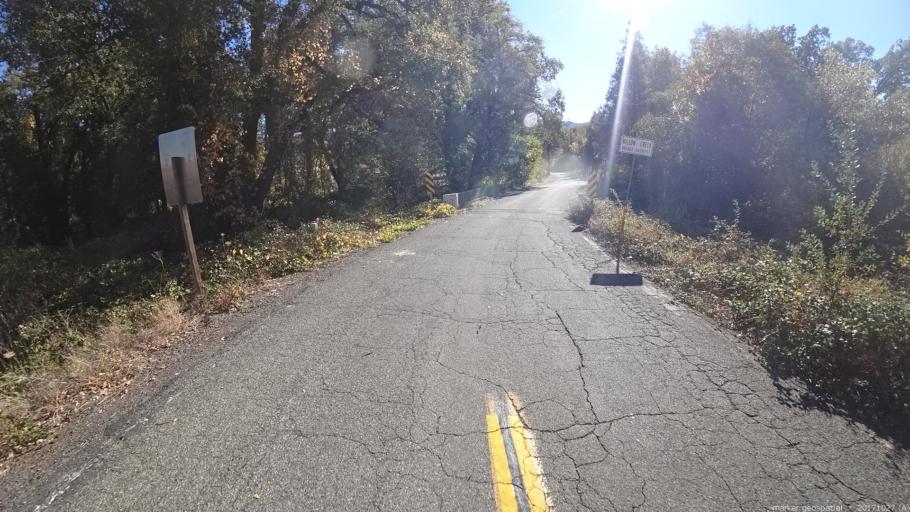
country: US
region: California
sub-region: Shasta County
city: Burney
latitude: 40.8242
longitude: -121.9329
